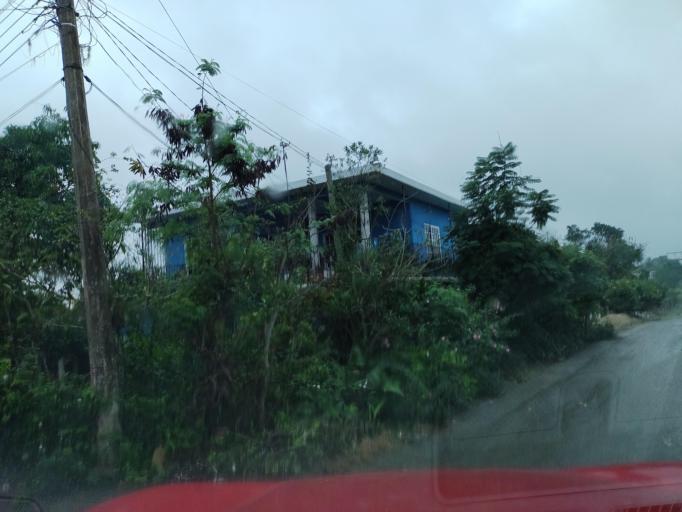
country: MX
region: Veracruz
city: Agua Dulce
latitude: 20.3324
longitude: -97.3270
